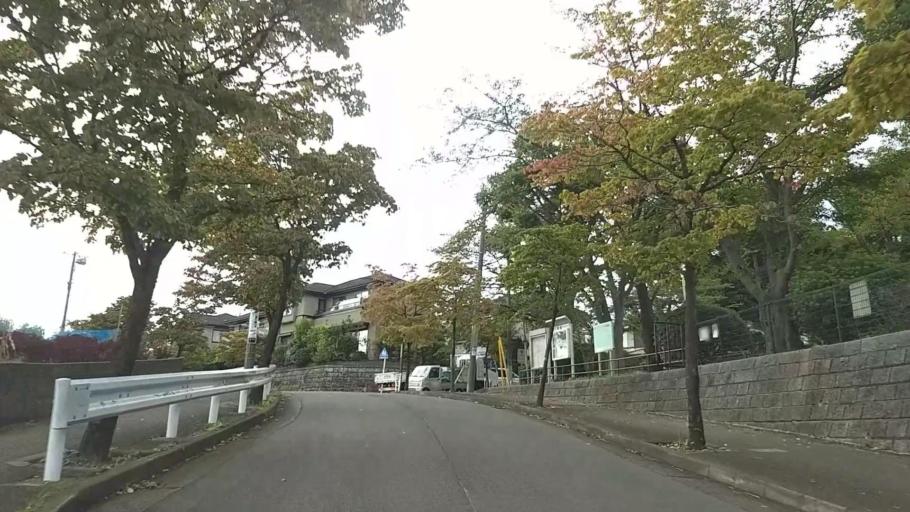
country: JP
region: Kanagawa
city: Yokohama
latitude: 35.4800
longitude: 139.5629
